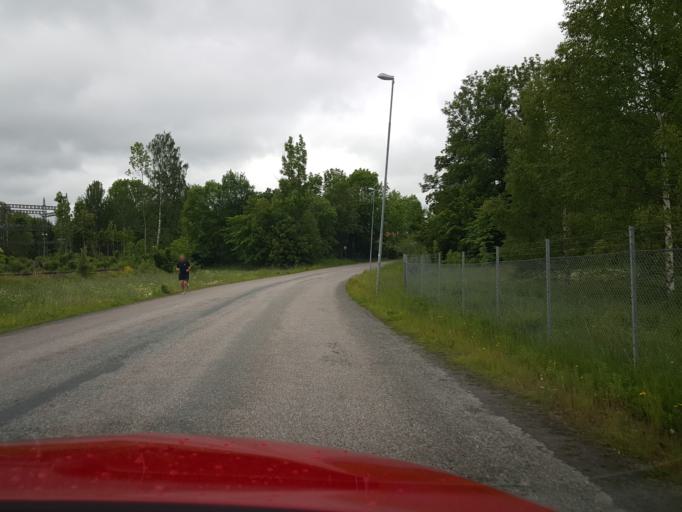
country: SE
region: Uppsala
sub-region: Osthammars Kommun
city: Gimo
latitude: 60.1740
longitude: 18.1739
